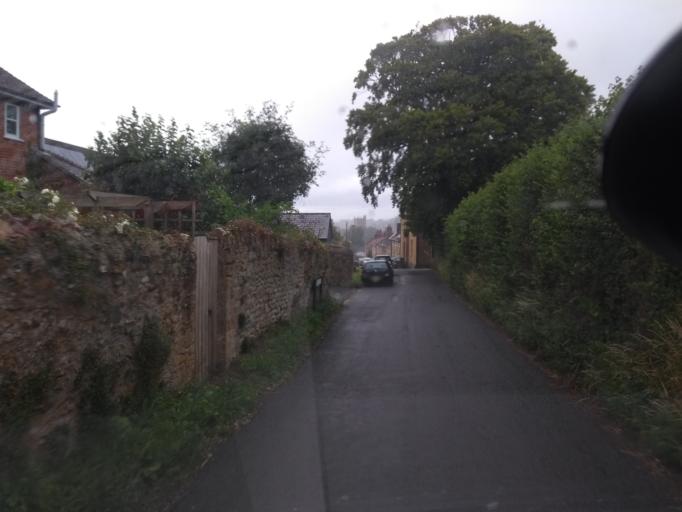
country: GB
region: England
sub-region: Somerset
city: Crewkerne
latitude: 50.8812
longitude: -2.8006
